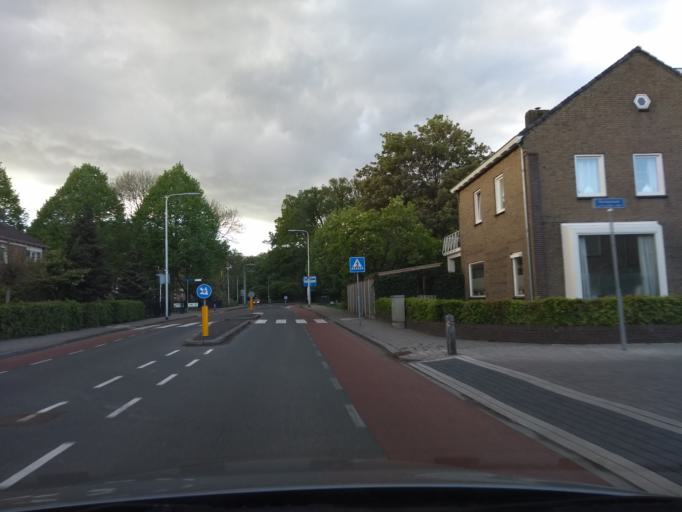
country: NL
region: Overijssel
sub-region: Gemeente Almelo
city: Almelo
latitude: 52.3546
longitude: 6.6721
